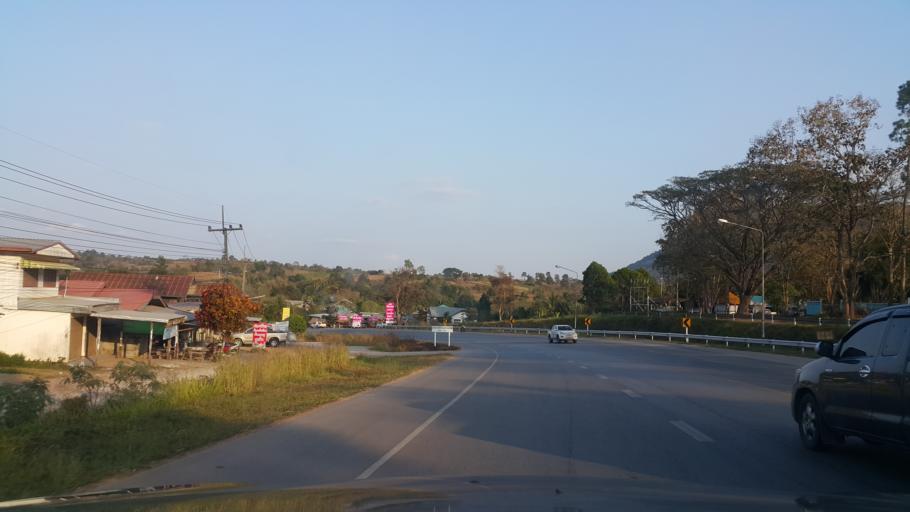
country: TH
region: Loei
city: Phu Ruea
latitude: 17.4568
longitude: 101.5043
